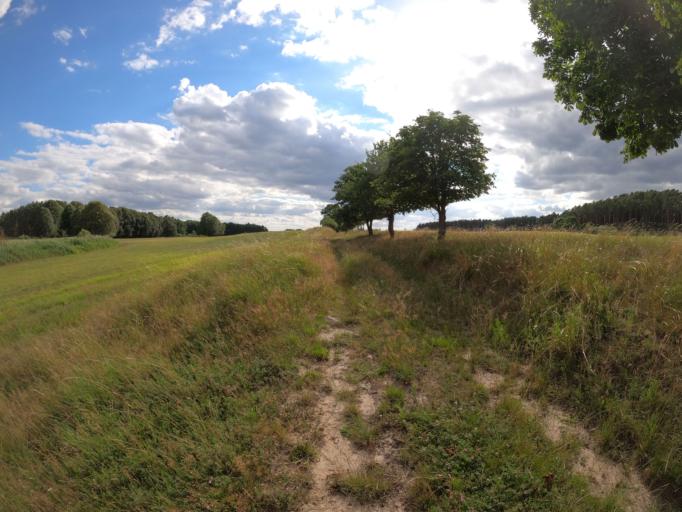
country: DE
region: Brandenburg
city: Angermunde
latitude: 53.0317
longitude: 13.9081
